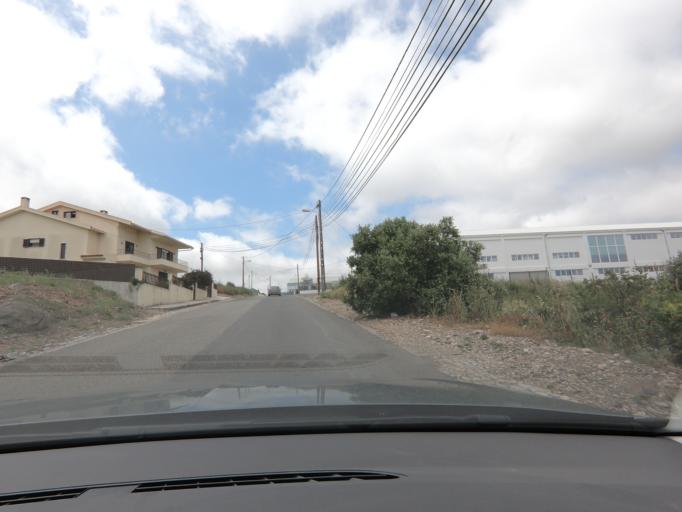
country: PT
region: Lisbon
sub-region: Oeiras
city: Porto Salvo
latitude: 38.7415
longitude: -9.3151
